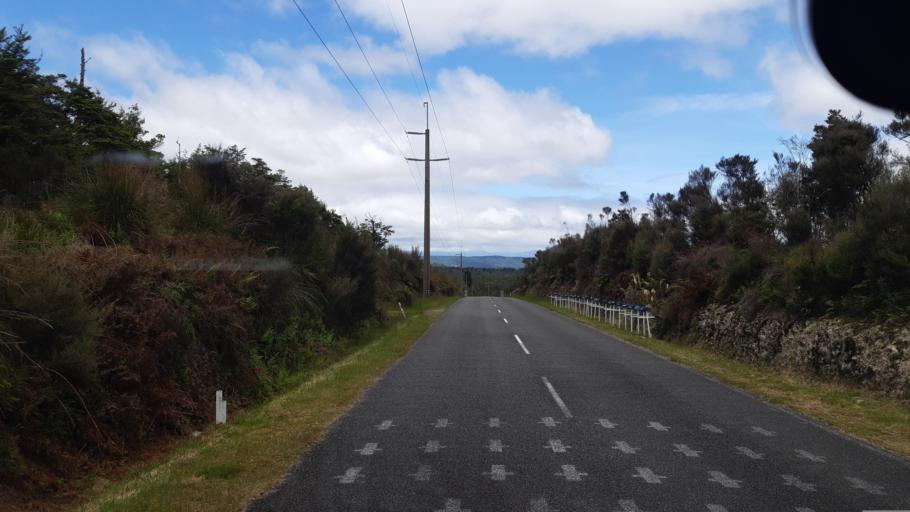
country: NZ
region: West Coast
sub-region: Grey District
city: Greymouth
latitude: -42.2587
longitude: 171.5465
